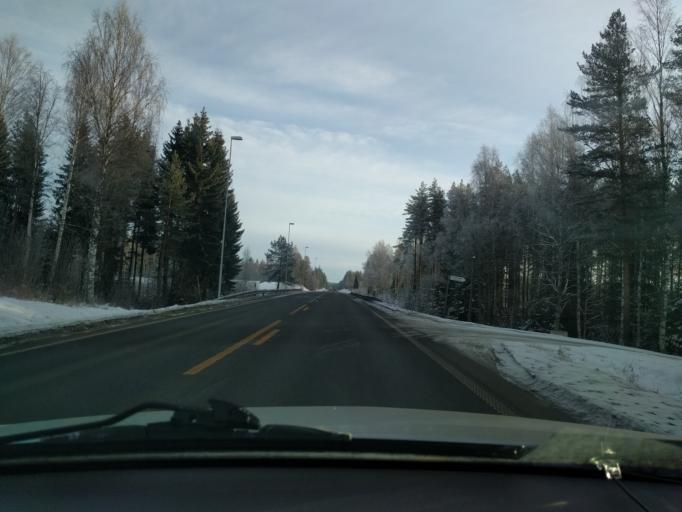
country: NO
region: Hedmark
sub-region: Elverum
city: Elverum
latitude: 60.9066
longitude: 11.6151
